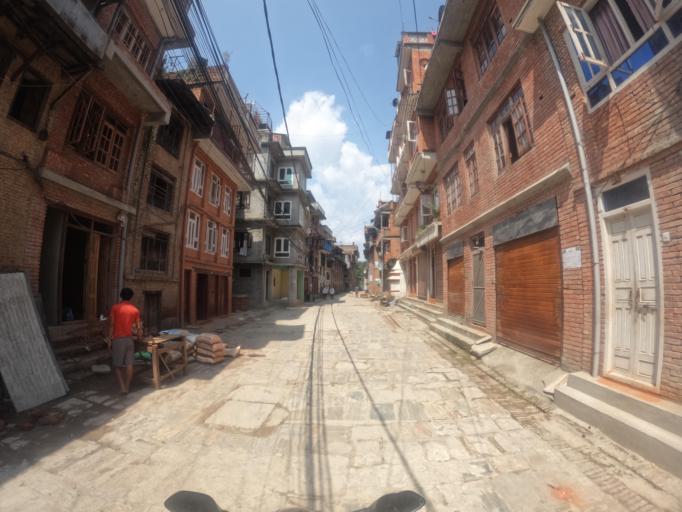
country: NP
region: Central Region
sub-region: Bagmati Zone
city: Bhaktapur
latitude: 27.6911
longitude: 85.3879
